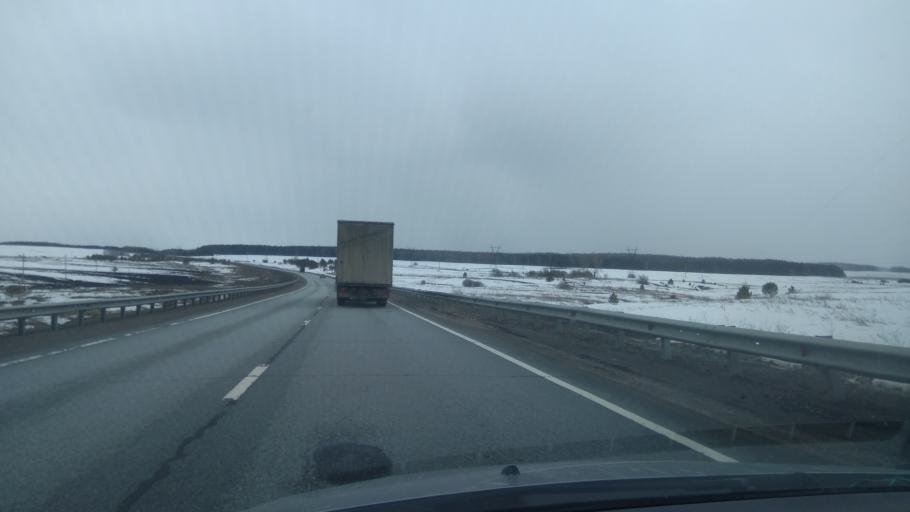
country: RU
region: Sverdlovsk
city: Achit
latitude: 56.8901
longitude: 57.6094
